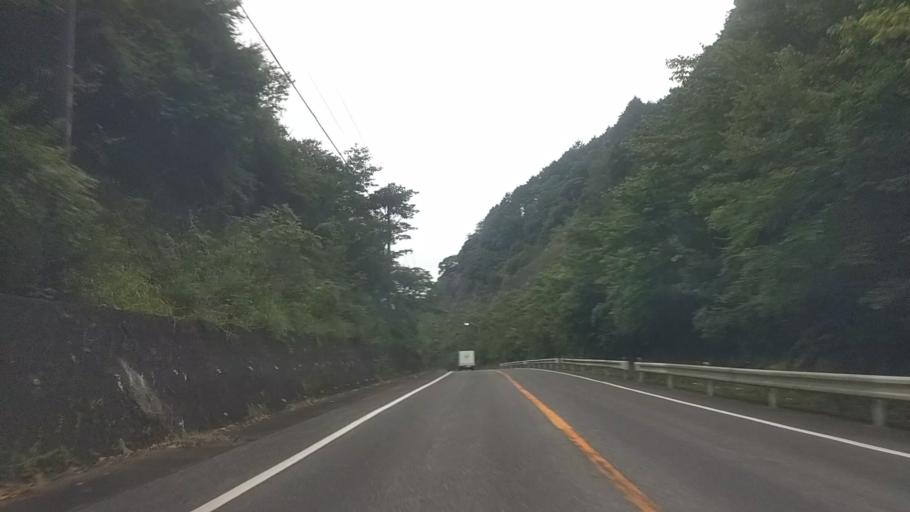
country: JP
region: Chiba
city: Kawaguchi
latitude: 35.1677
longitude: 140.0601
